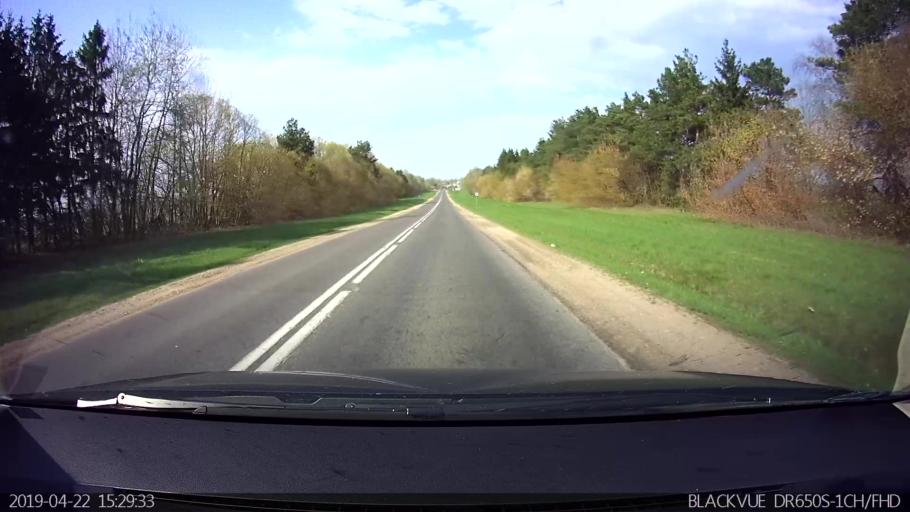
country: BY
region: Brest
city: Vysokaye
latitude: 52.3880
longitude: 23.3743
